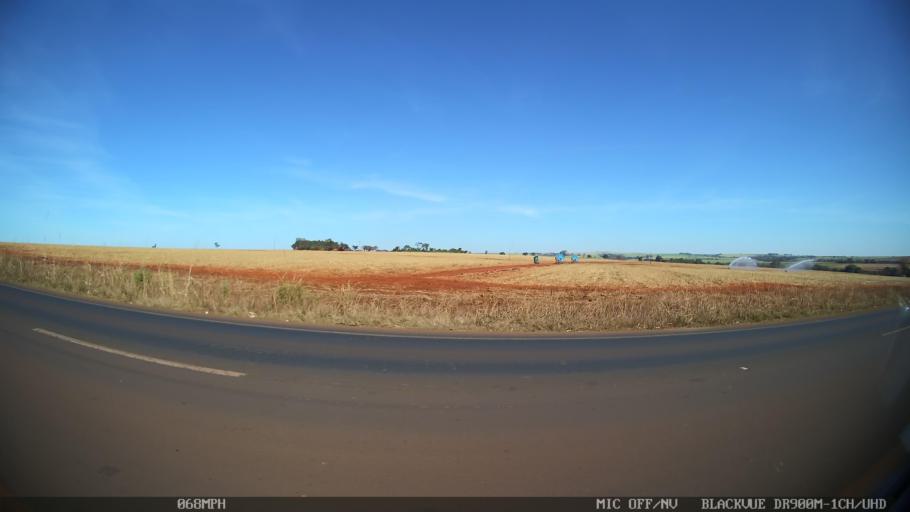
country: BR
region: Sao Paulo
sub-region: Sao Joaquim Da Barra
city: Sao Joaquim da Barra
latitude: -20.5177
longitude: -47.8766
